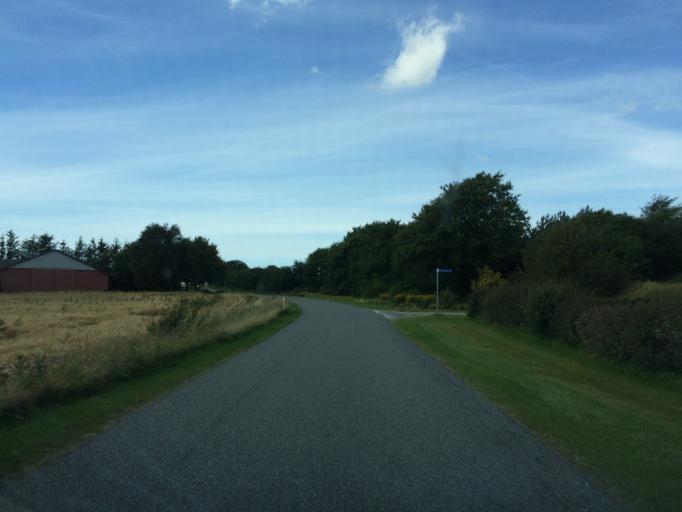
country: DK
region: Central Jutland
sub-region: Ringkobing-Skjern Kommune
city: Skjern
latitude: 56.0166
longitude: 8.4131
